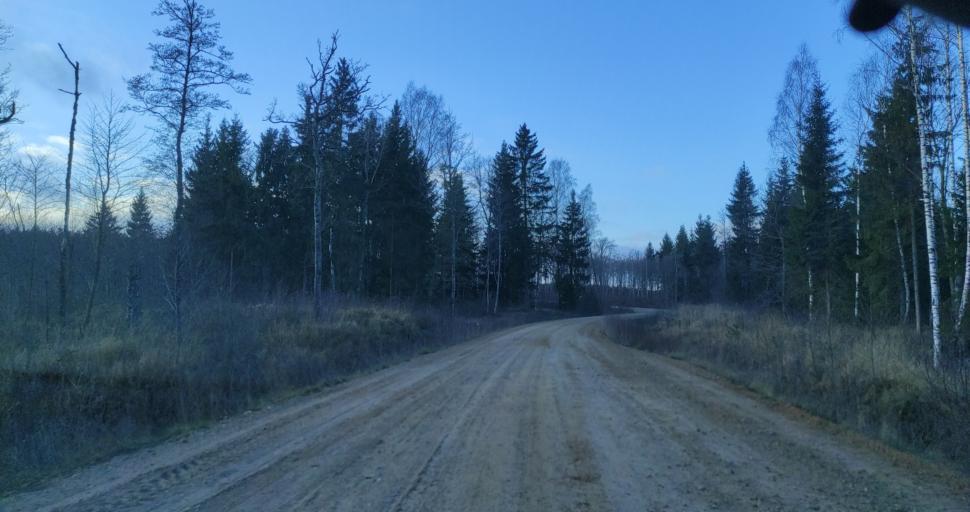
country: LV
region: Kuldigas Rajons
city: Kuldiga
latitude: 57.0540
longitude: 21.8459
